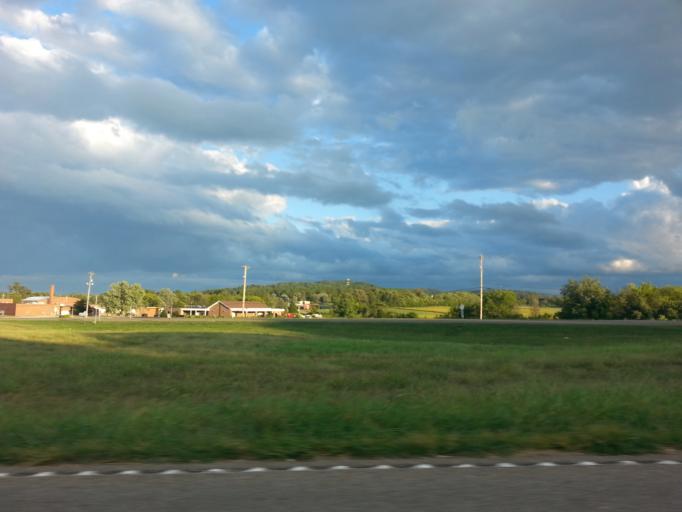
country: US
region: Tennessee
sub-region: Jefferson County
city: Jefferson City
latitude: 36.1103
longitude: -83.5168
